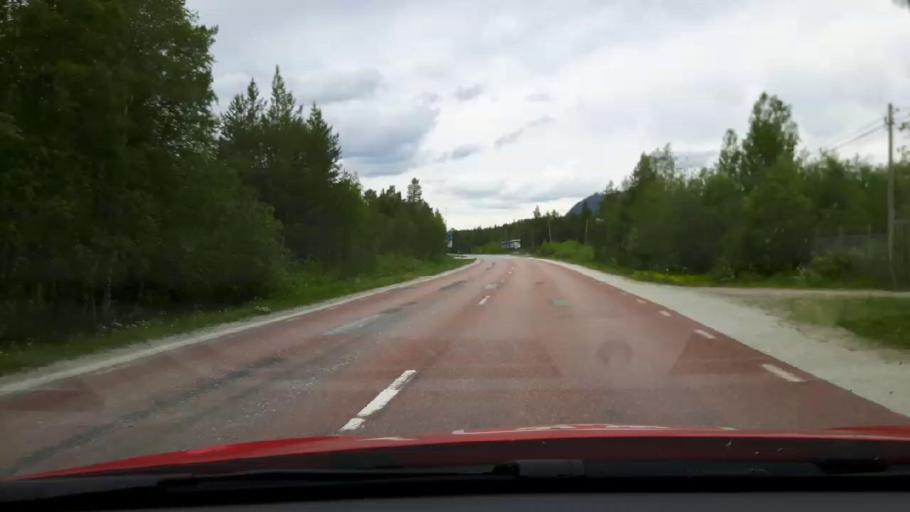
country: NO
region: Hedmark
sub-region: Engerdal
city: Engerdal
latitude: 62.5221
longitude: 12.5912
